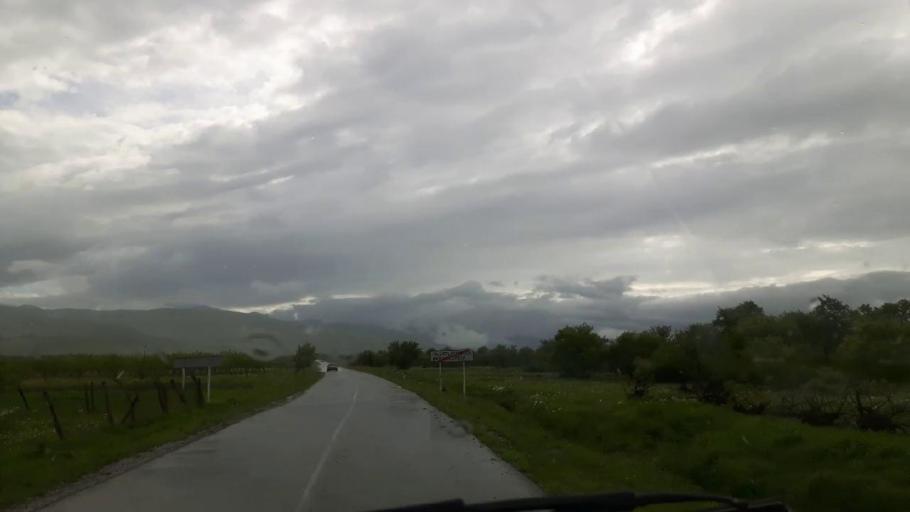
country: GE
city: Agara
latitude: 42.0024
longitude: 43.7569
